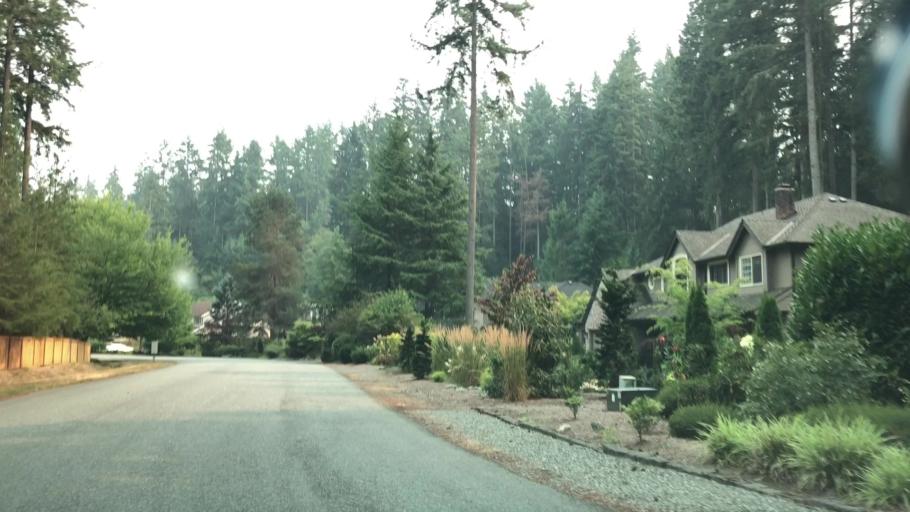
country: US
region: Washington
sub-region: King County
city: Cottage Lake
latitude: 47.7741
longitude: -122.0929
